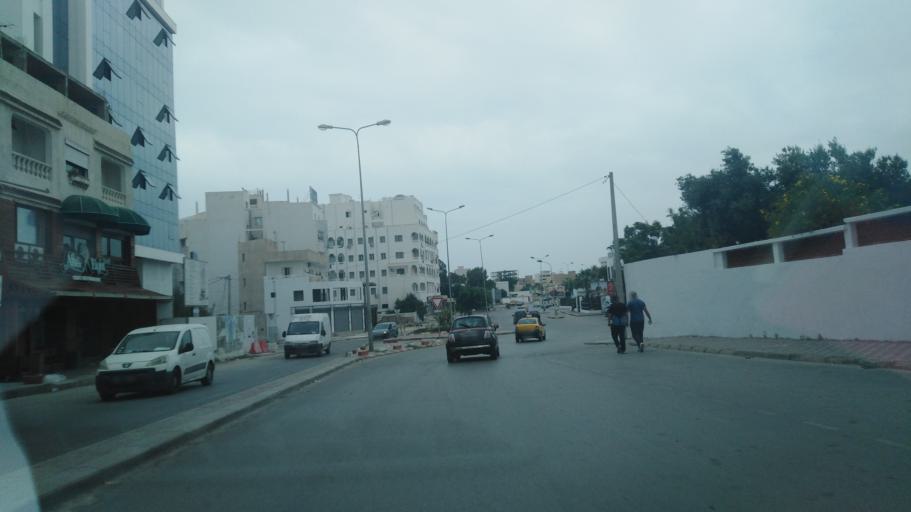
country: TN
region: Susah
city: Sousse
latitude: 35.8309
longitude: 10.6275
